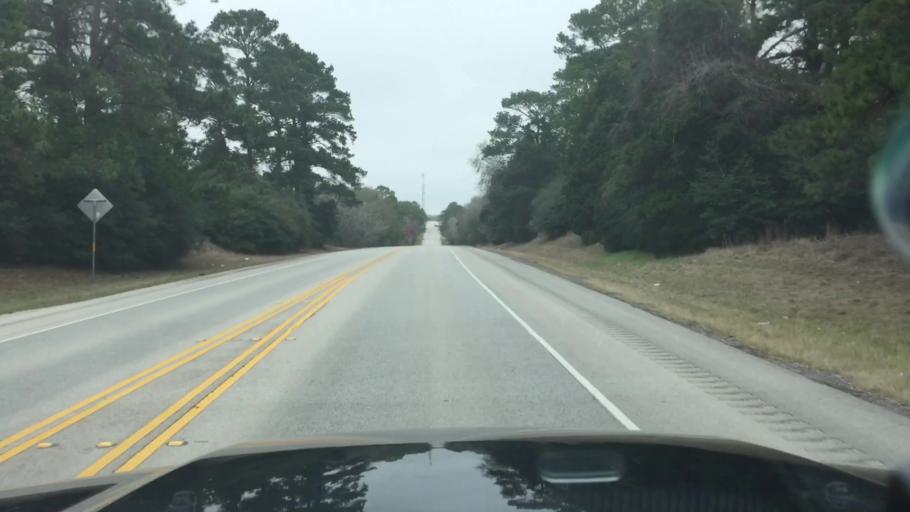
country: US
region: Texas
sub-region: Fayette County
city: La Grange
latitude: 30.0095
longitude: -96.8952
